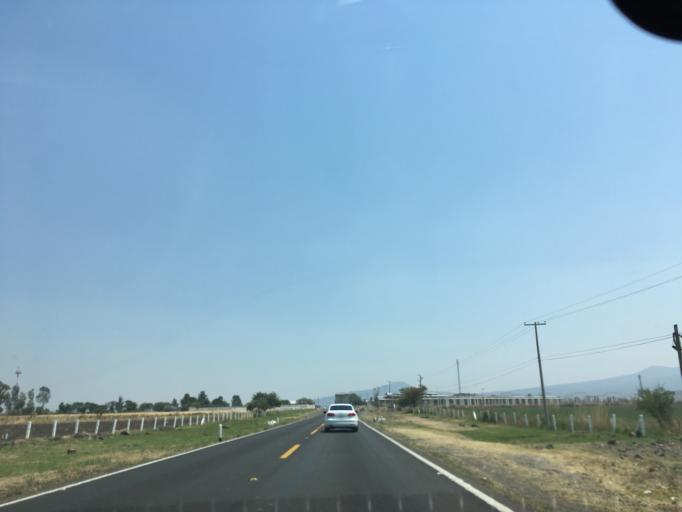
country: MX
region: Michoacan
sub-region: Cuitzeo
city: Cuamio
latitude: 20.0507
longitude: -101.1507
